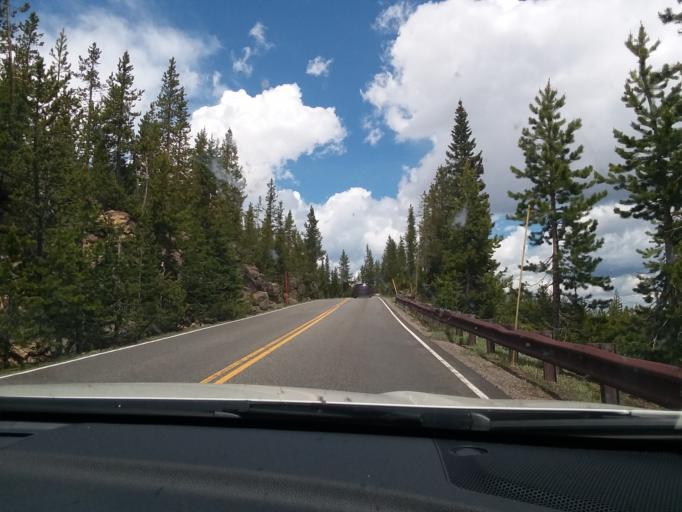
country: US
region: Montana
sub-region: Gallatin County
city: West Yellowstone
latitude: 44.1977
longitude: -110.6585
